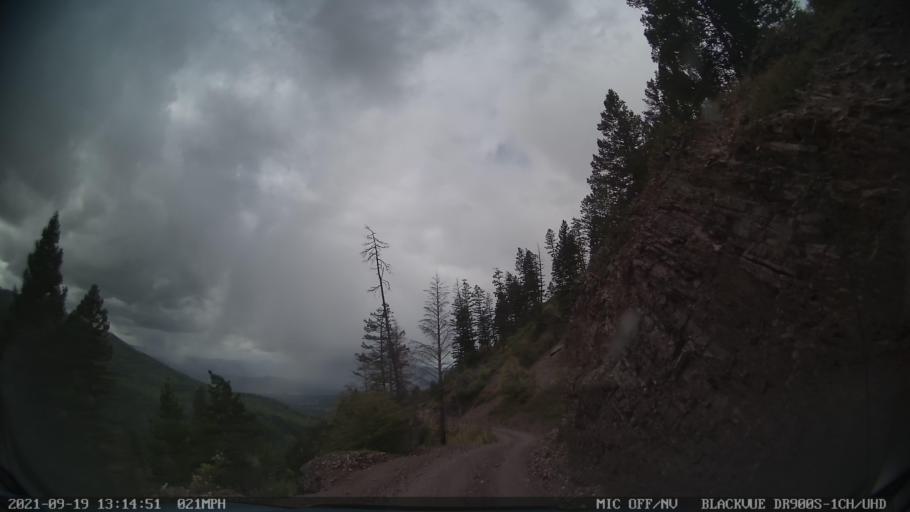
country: US
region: Montana
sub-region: Missoula County
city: Seeley Lake
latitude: 47.1787
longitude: -113.3654
